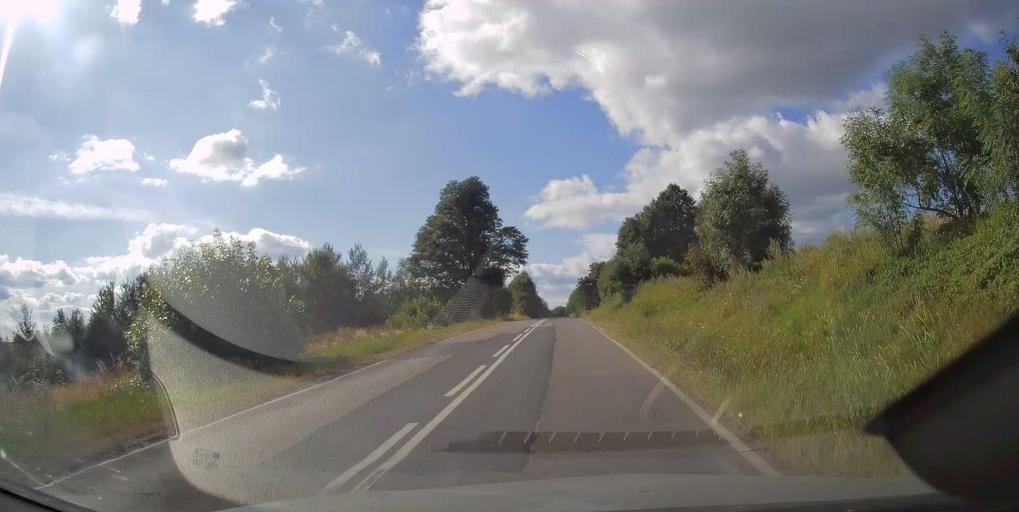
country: PL
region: Swietokrzyskie
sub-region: Powiat skarzyski
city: Suchedniow
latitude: 50.9878
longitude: 20.8661
